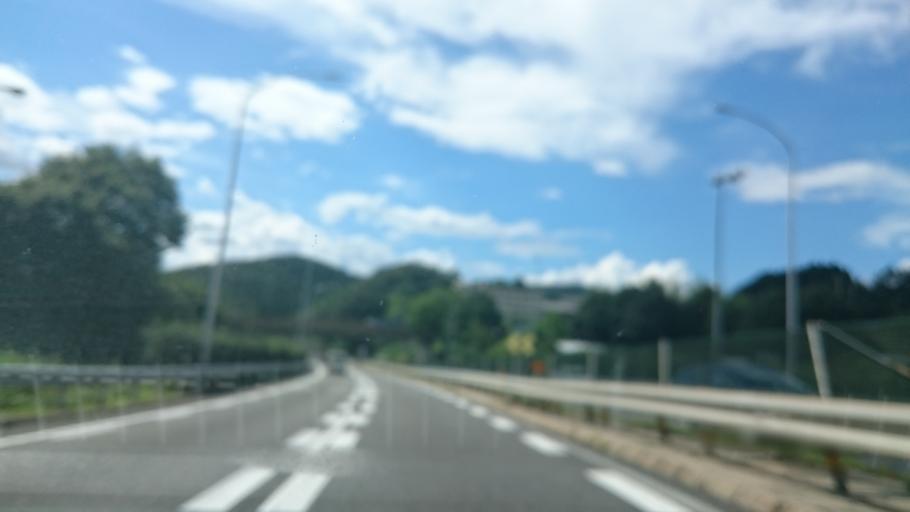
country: JP
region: Gifu
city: Nakatsugawa
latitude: 35.5177
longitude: 137.5721
